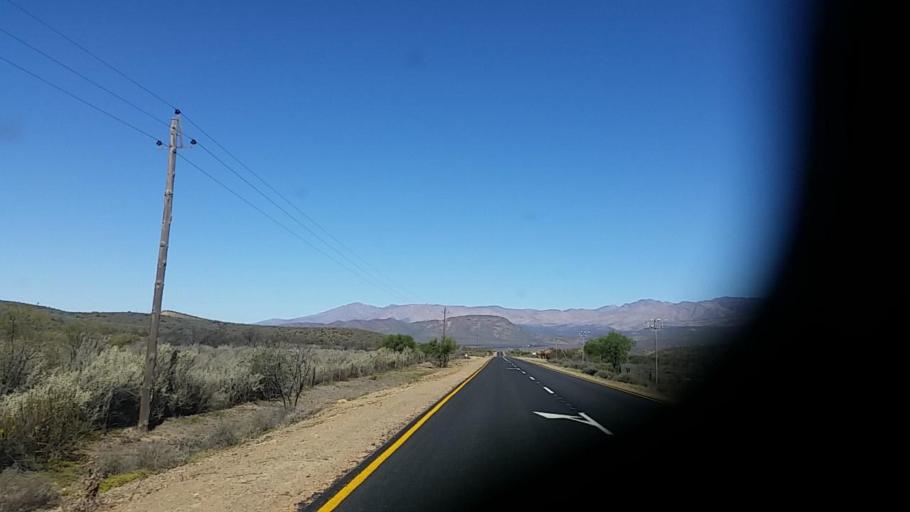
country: ZA
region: Western Cape
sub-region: Eden District Municipality
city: Oudtshoorn
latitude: -33.4798
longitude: 22.6545
